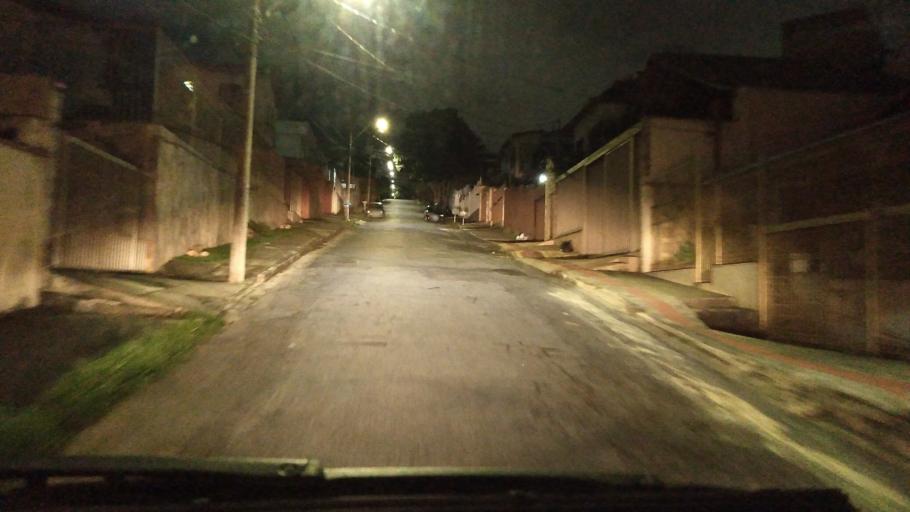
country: BR
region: Minas Gerais
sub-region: Belo Horizonte
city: Belo Horizonte
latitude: -19.8924
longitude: -43.9719
